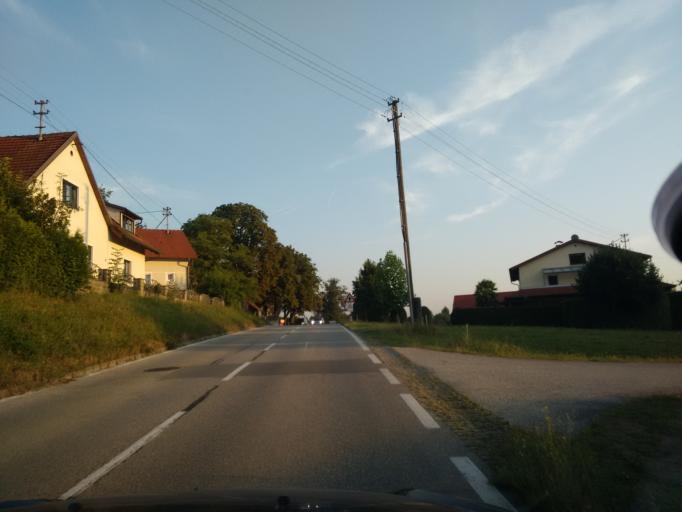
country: AT
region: Upper Austria
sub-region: Politischer Bezirk Grieskirchen
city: Bad Schallerbach
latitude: 48.1894
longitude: 13.9544
